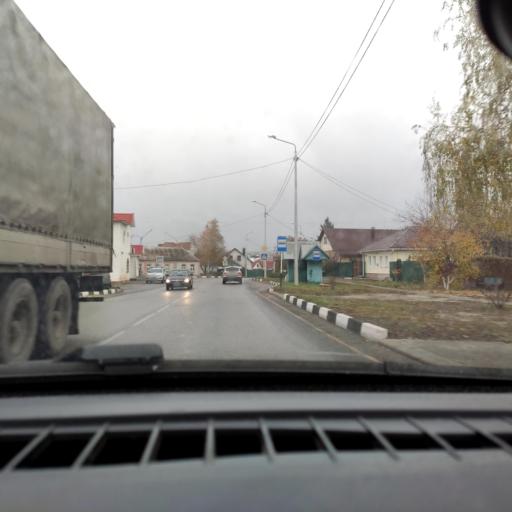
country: RU
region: Belgorod
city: Alekseyevka
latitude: 50.6335
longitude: 38.7005
